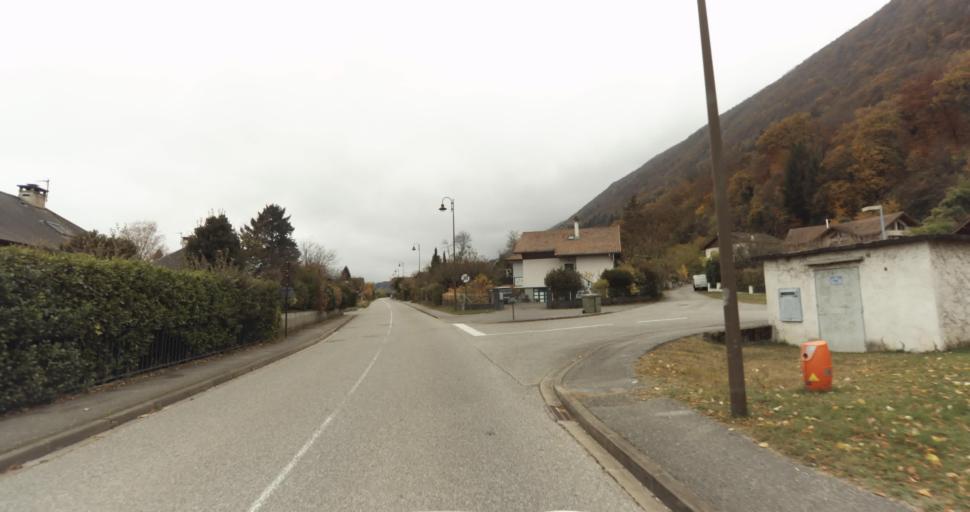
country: FR
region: Rhone-Alpes
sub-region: Departement de la Haute-Savoie
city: Sevrier
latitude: 45.8587
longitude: 6.1382
